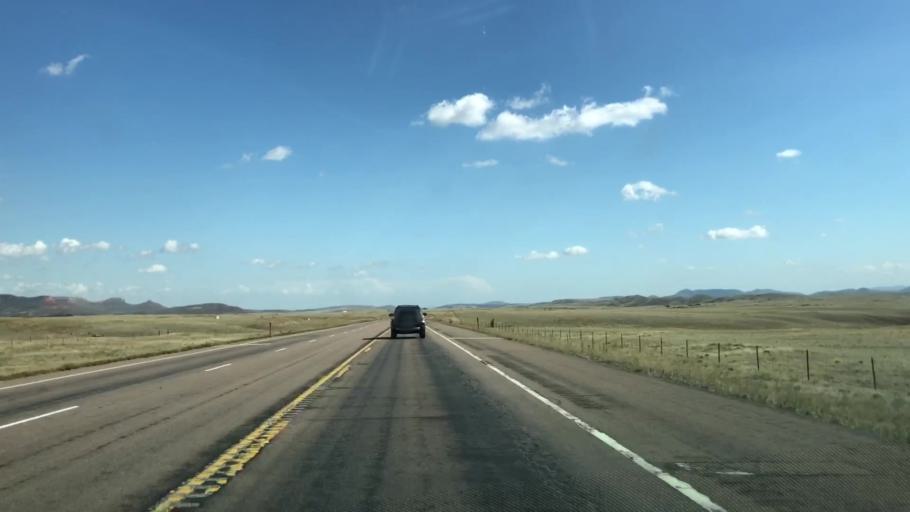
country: US
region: Colorado
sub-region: Larimer County
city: Laporte
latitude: 40.9076
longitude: -105.3105
